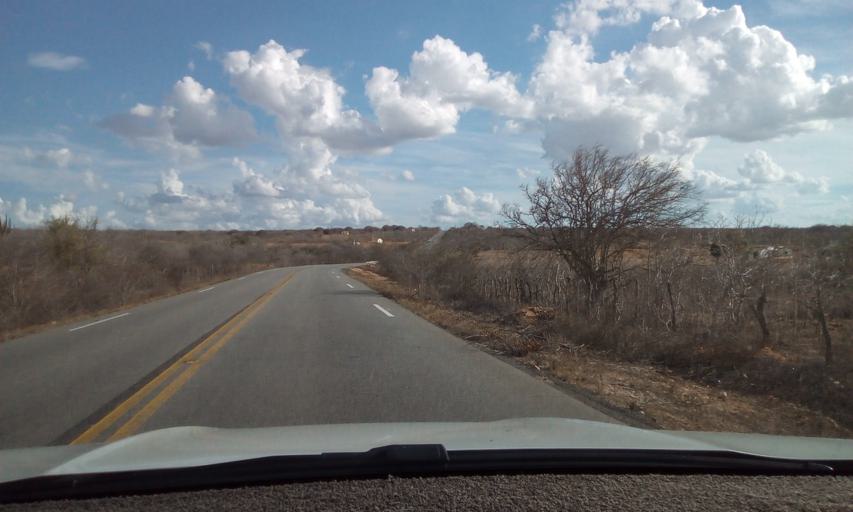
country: BR
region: Paraiba
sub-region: Soledade
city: Soledade
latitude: -6.8756
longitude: -36.3997
